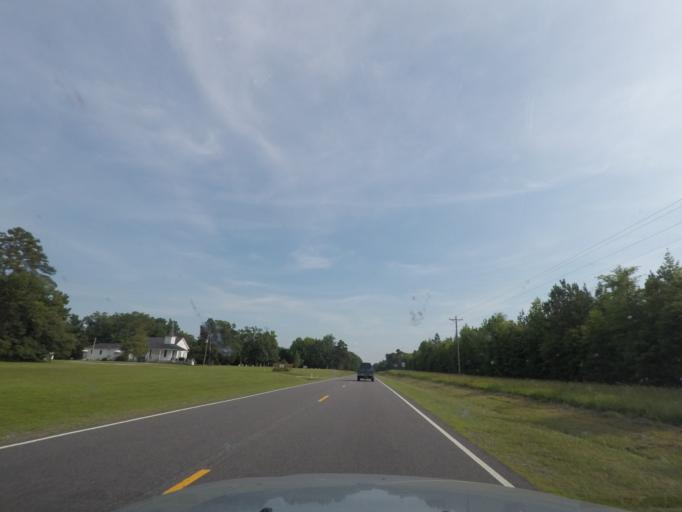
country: US
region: Virginia
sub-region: Mecklenburg County
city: Clarksville
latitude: 36.7218
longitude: -78.6305
